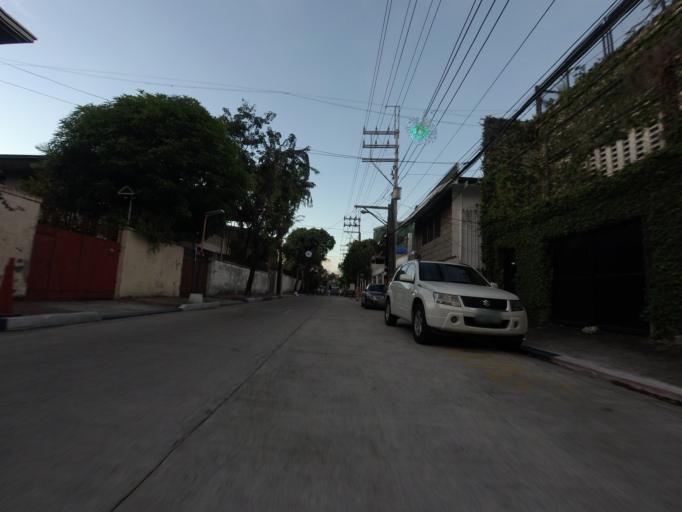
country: PH
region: Metro Manila
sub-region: City of Manila
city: Quiapo
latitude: 14.5948
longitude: 120.9923
